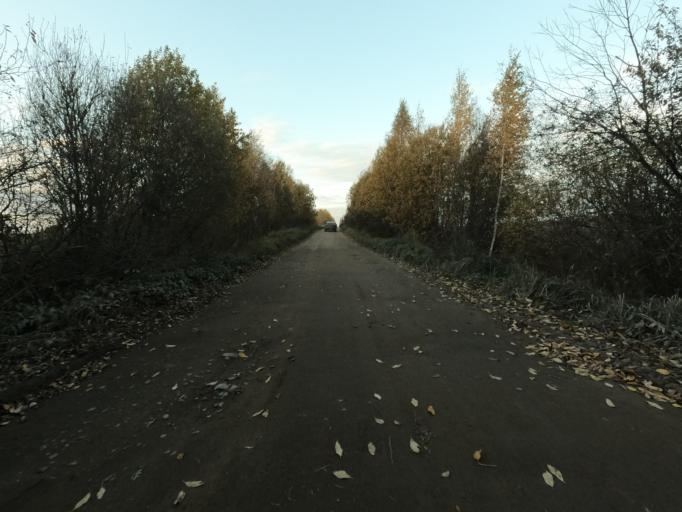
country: RU
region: Leningrad
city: Mga
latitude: 59.7909
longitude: 31.2014
